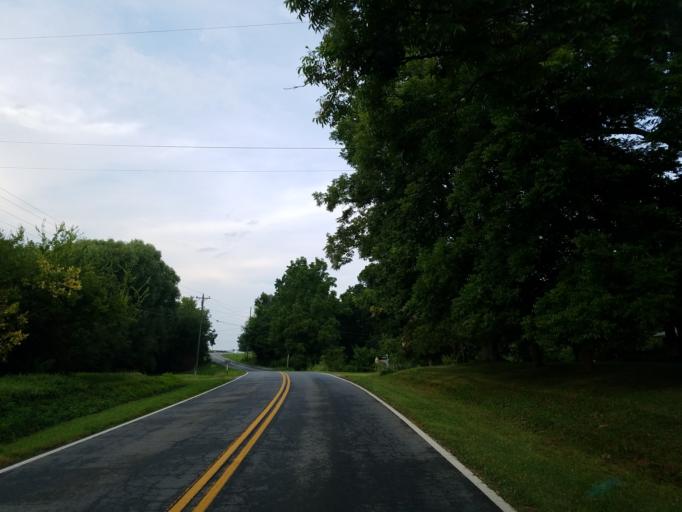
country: US
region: Georgia
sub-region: Pickens County
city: Jasper
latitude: 34.4605
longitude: -84.5305
